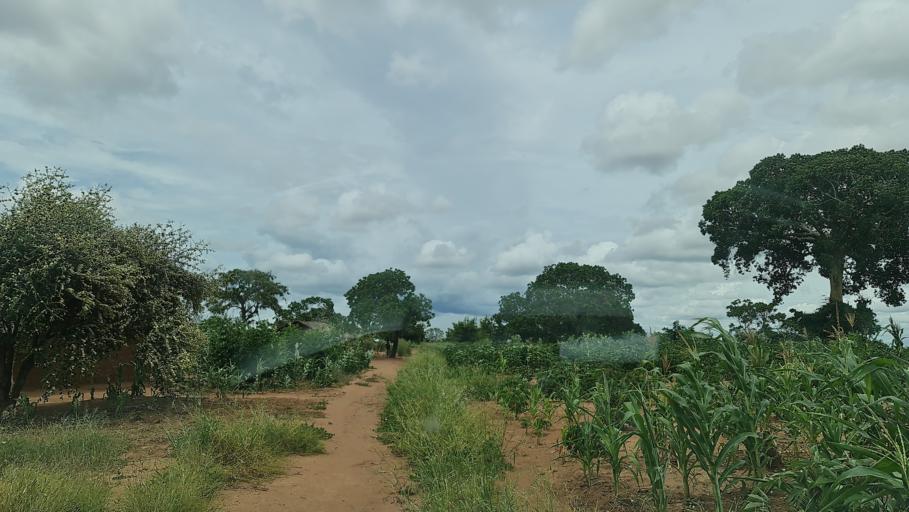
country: MZ
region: Nampula
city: Nacala
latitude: -14.7807
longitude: 39.9860
